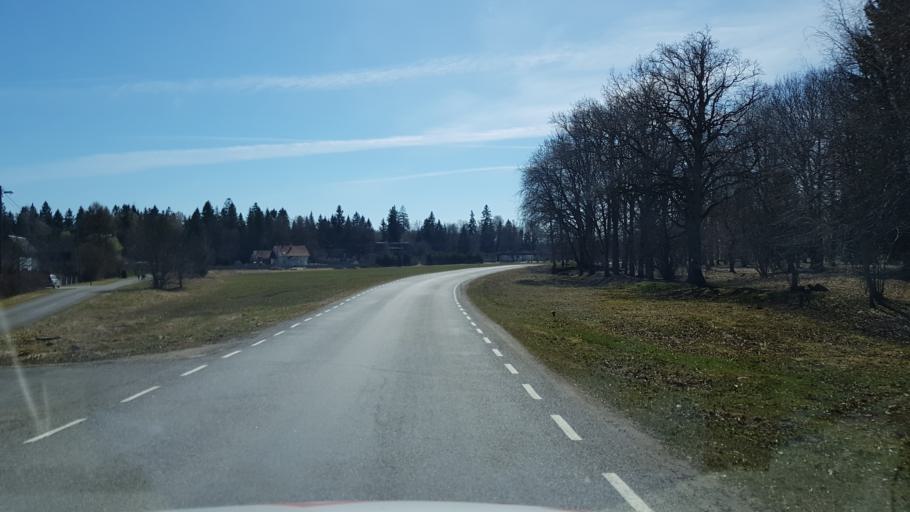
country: EE
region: Laeaene-Virumaa
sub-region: Vinni vald
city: Vinni
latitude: 59.2878
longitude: 26.4269
